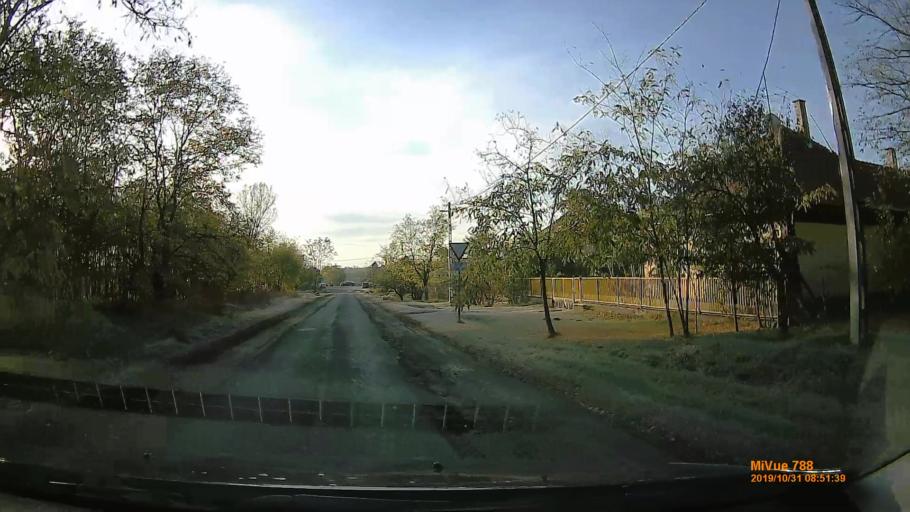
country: HU
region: Pest
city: Albertirsa
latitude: 47.2638
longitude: 19.6071
